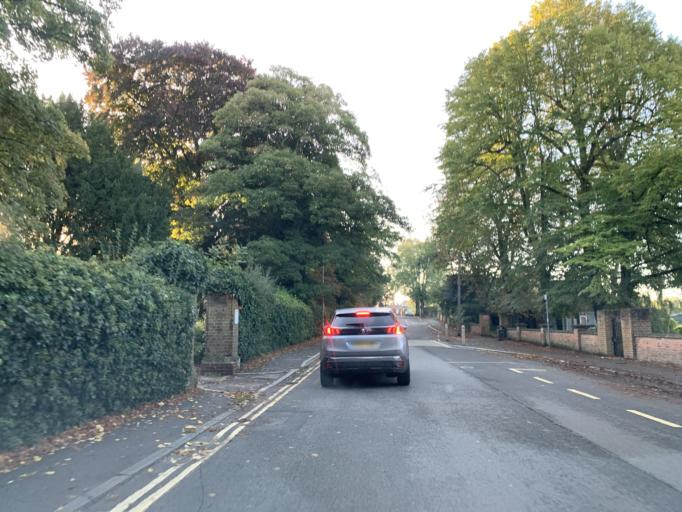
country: GB
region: England
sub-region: Wiltshire
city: Salisbury
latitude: 51.0800
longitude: -1.7988
